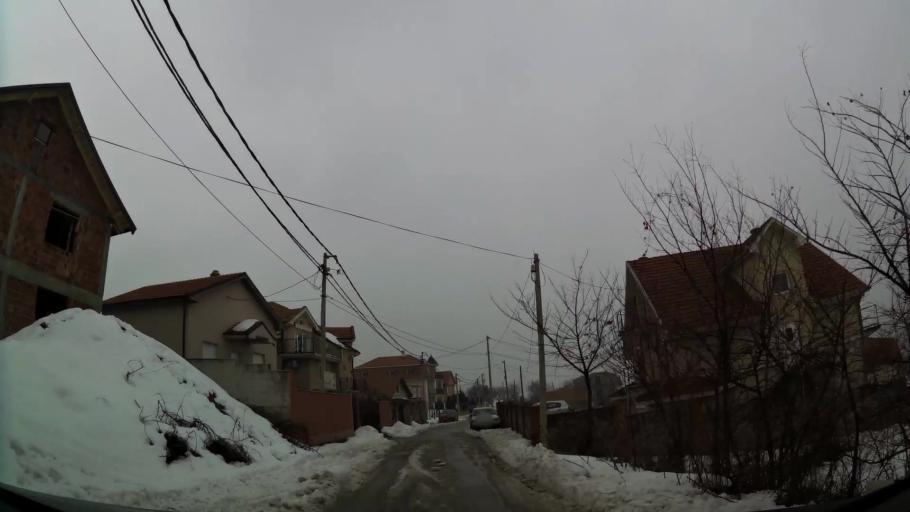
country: RS
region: Central Serbia
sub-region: Belgrade
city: Zvezdara
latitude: 44.7522
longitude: 20.5287
